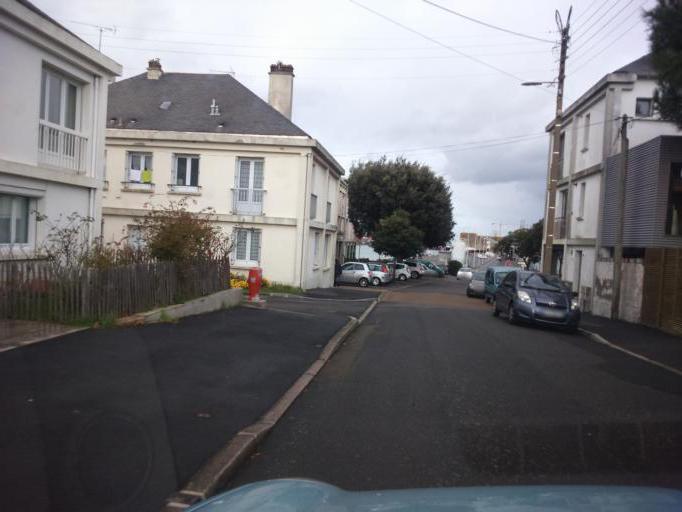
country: FR
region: Pays de la Loire
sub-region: Departement de la Loire-Atlantique
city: Saint-Nazaire
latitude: 47.2716
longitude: -2.2004
